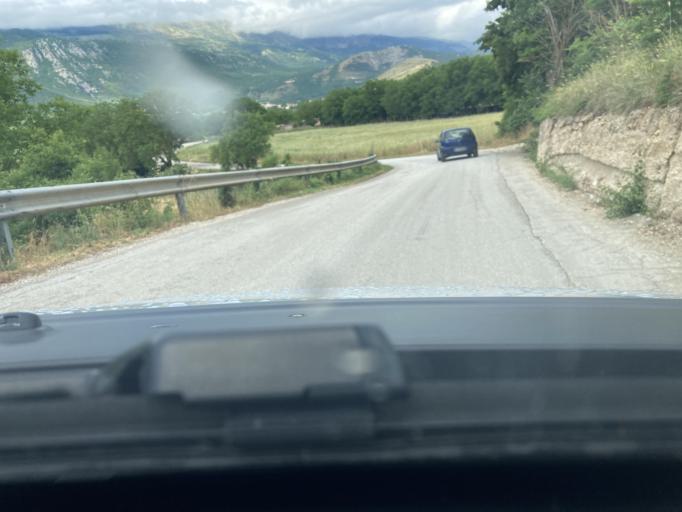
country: IT
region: Abruzzo
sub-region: Provincia dell' Aquila
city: San Demetrio Ne' Vestini
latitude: 42.2941
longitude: 13.5502
